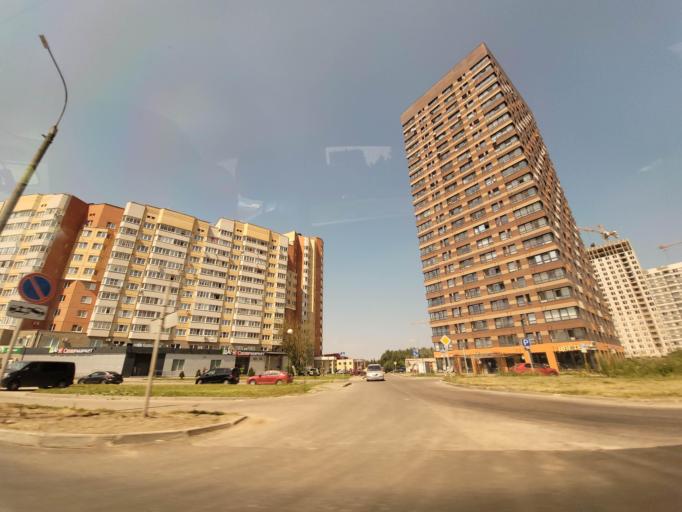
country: RU
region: Kaluga
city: Obninsk
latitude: 55.1237
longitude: 36.6104
